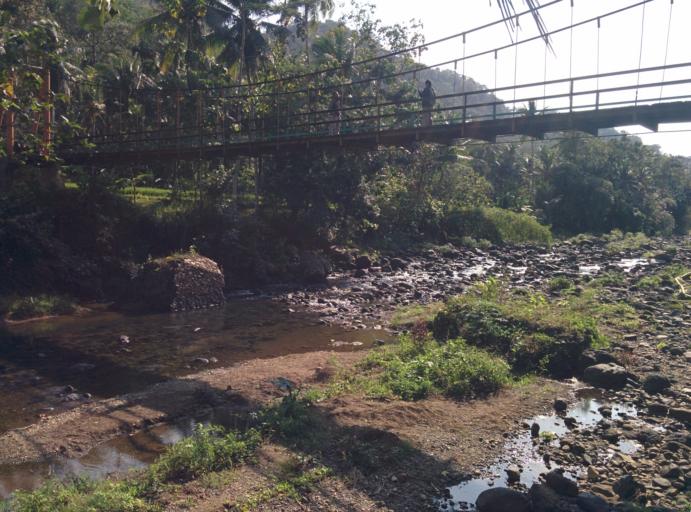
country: ID
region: East Java
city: Gajahrejo Krajan
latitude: -8.3457
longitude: 112.6755
